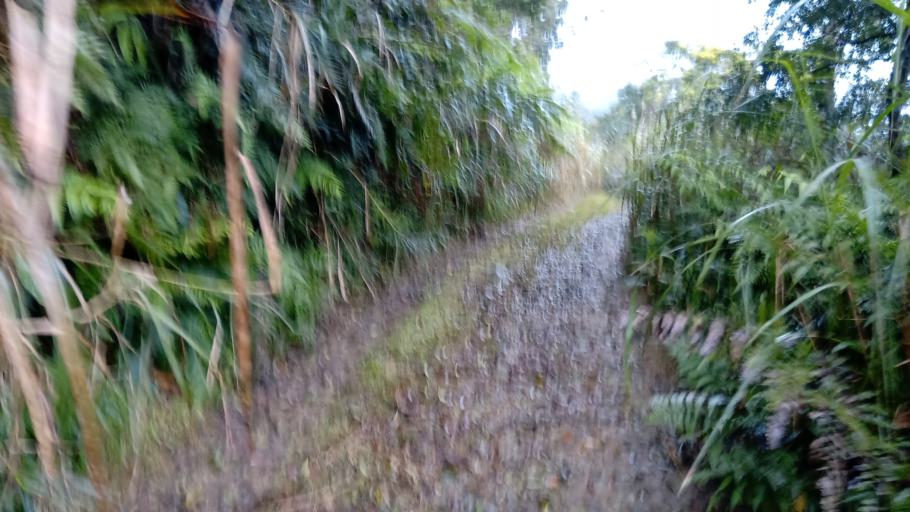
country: TW
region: Taiwan
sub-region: Yilan
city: Yilan
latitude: 24.8168
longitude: 121.6897
